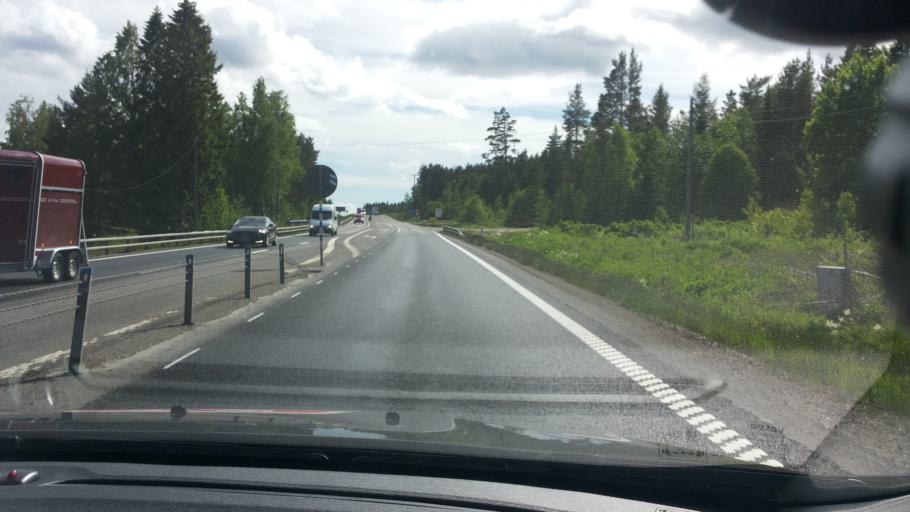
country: SE
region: Vaesternorrland
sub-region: Sundsvalls Kommun
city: Njurundabommen
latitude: 62.1560
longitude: 17.3504
